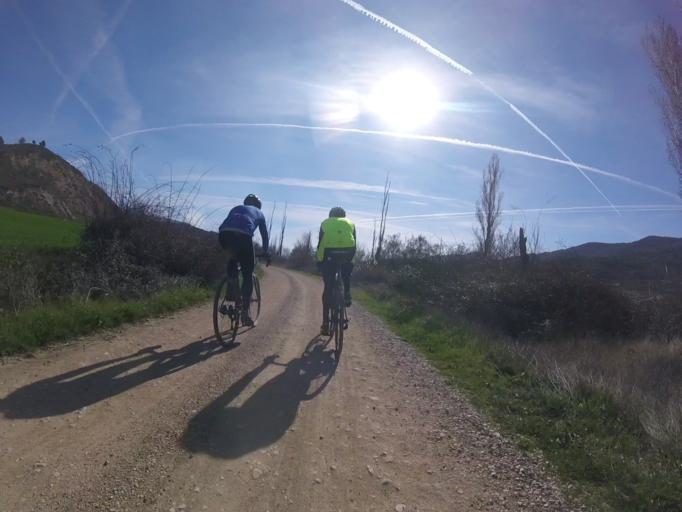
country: ES
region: Navarre
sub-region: Provincia de Navarra
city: Cirauqui
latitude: 42.6719
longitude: -1.9117
